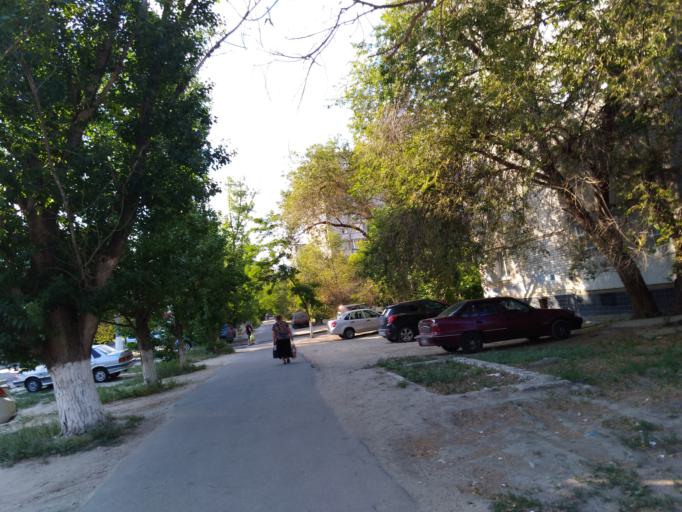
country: RU
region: Volgograd
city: Volgograd
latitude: 48.7191
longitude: 44.5159
